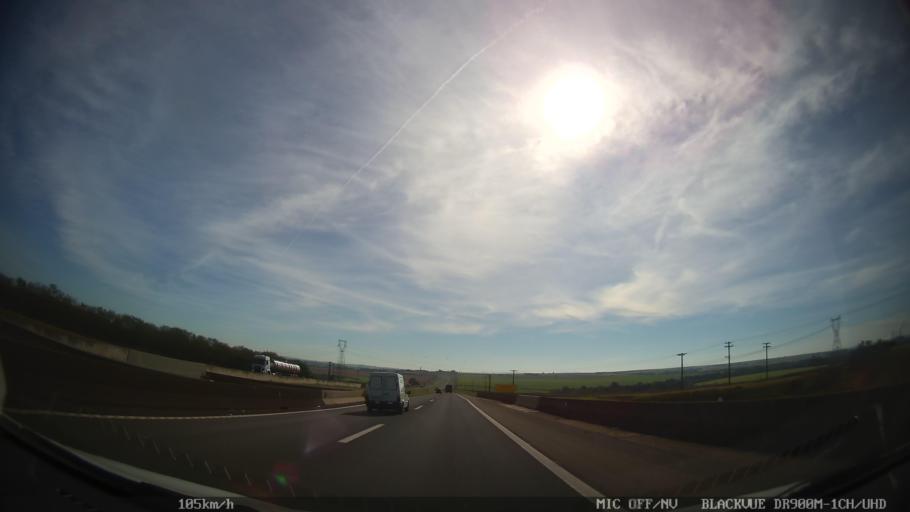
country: BR
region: Sao Paulo
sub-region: Cordeiropolis
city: Cordeiropolis
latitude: -22.4371
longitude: -47.3959
